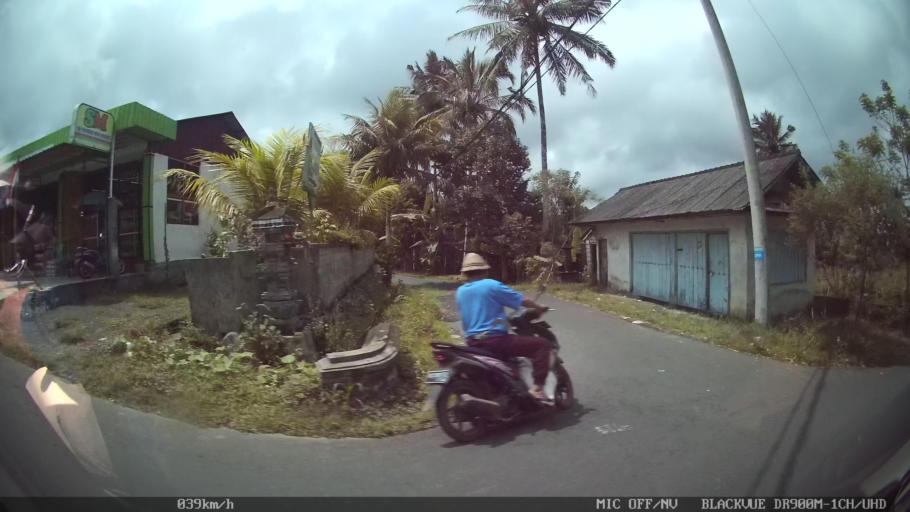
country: ID
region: Bali
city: Banjar Geriana Kangin
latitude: -8.4192
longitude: 115.4367
